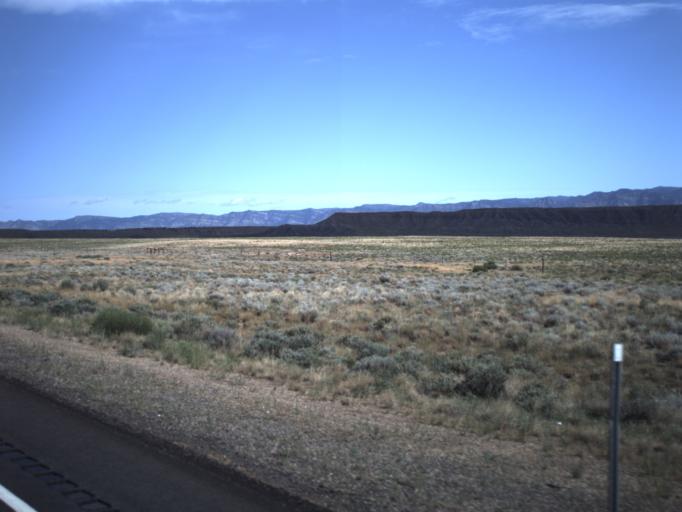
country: US
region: Utah
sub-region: Carbon County
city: East Carbon City
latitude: 39.4803
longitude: -110.5095
